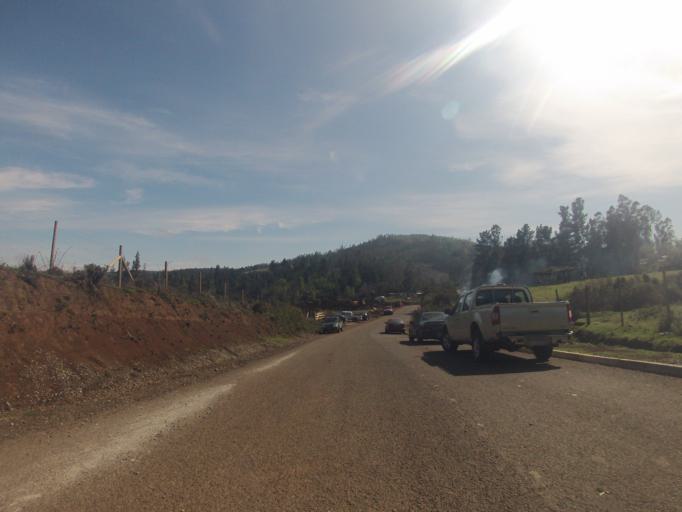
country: CL
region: Araucania
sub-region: Provincia de Cautin
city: Temuco
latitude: -38.6918
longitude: -72.5888
